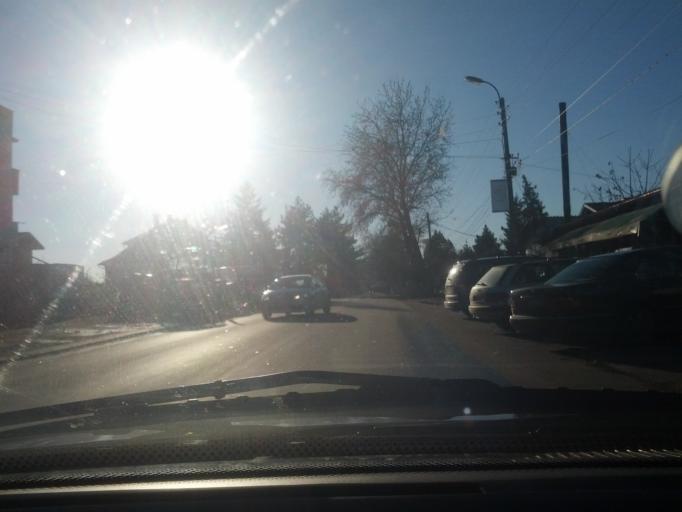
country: BG
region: Vratsa
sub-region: Obshtina Miziya
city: Miziya
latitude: 43.6913
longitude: 23.8115
